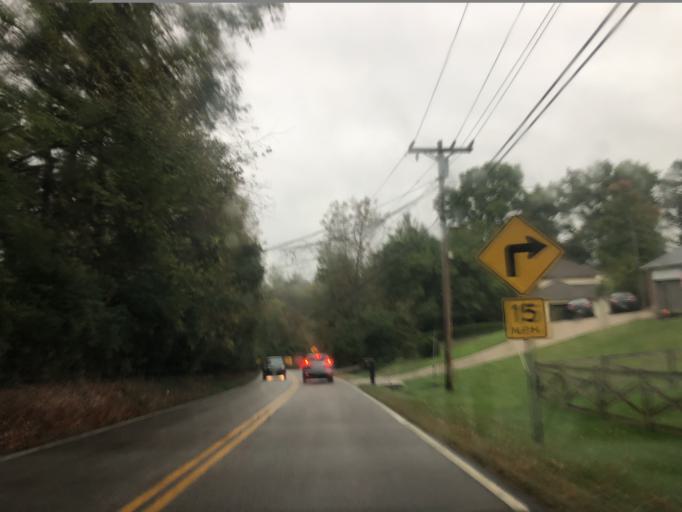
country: US
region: Ohio
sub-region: Clermont County
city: Mulberry
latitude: 39.2035
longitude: -84.2493
